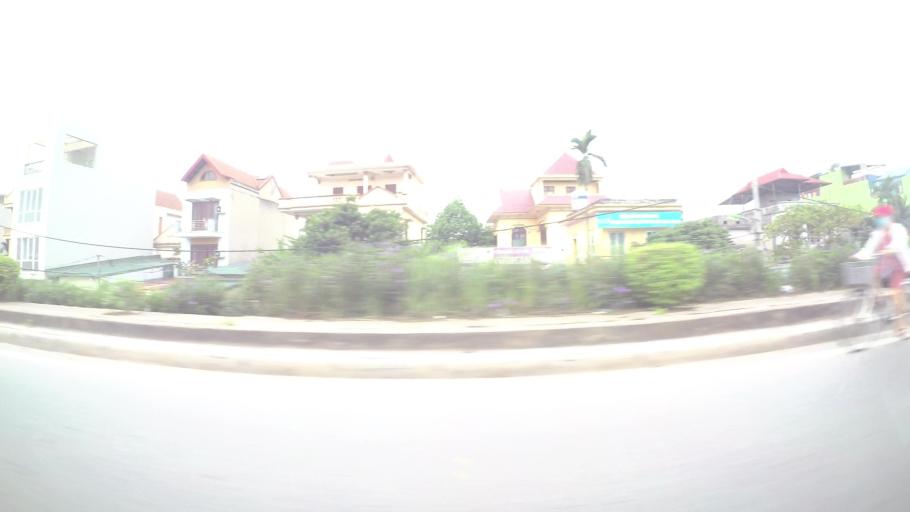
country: VN
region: Ha Noi
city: Hoan Kiem
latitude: 21.0589
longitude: 105.8642
